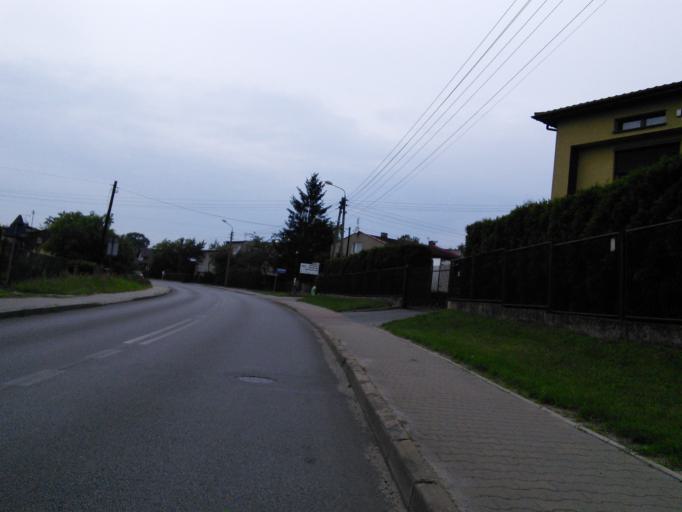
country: PL
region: Silesian Voivodeship
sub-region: Powiat bedzinski
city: Bobrowniki
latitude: 50.3744
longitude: 18.9757
